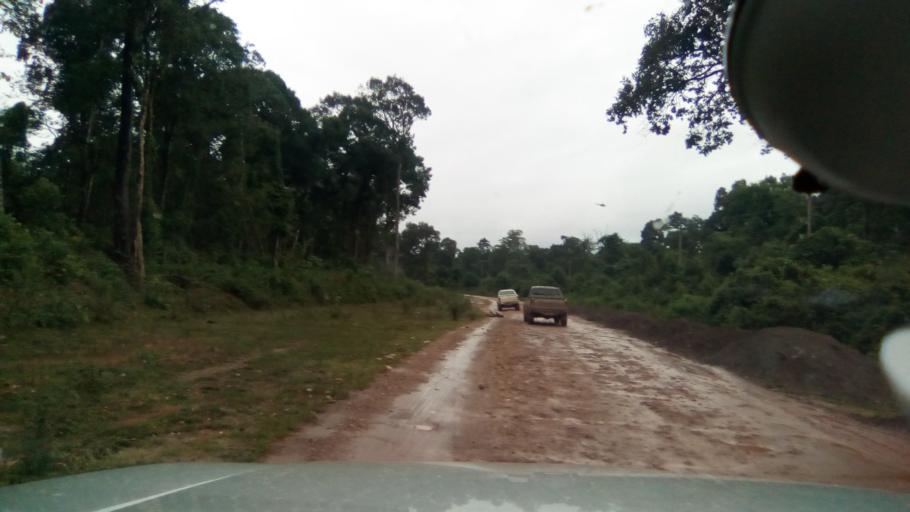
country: LA
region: Attapu
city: Attapu
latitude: 14.6786
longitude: 106.5590
